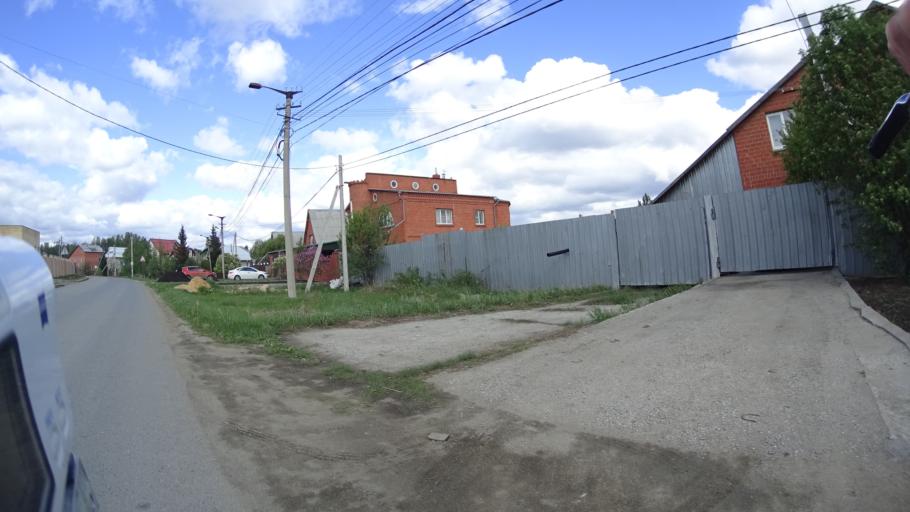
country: RU
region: Chelyabinsk
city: Sargazy
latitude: 55.1470
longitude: 61.2365
